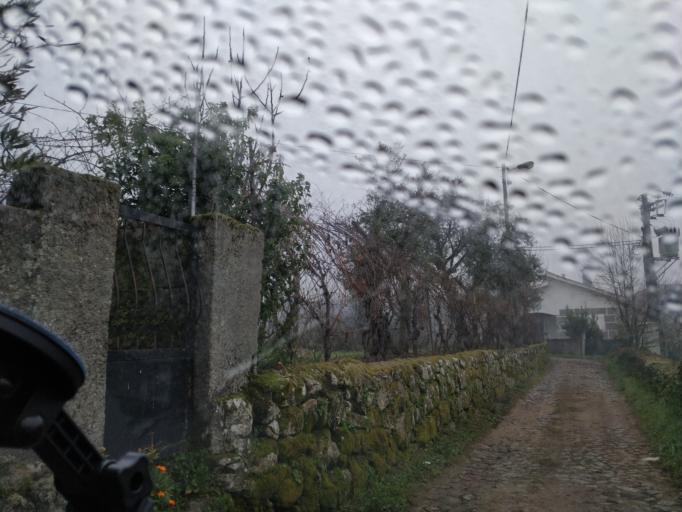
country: PT
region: Vila Real
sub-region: Vila Real
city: Vila Real
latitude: 41.3424
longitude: -7.7245
